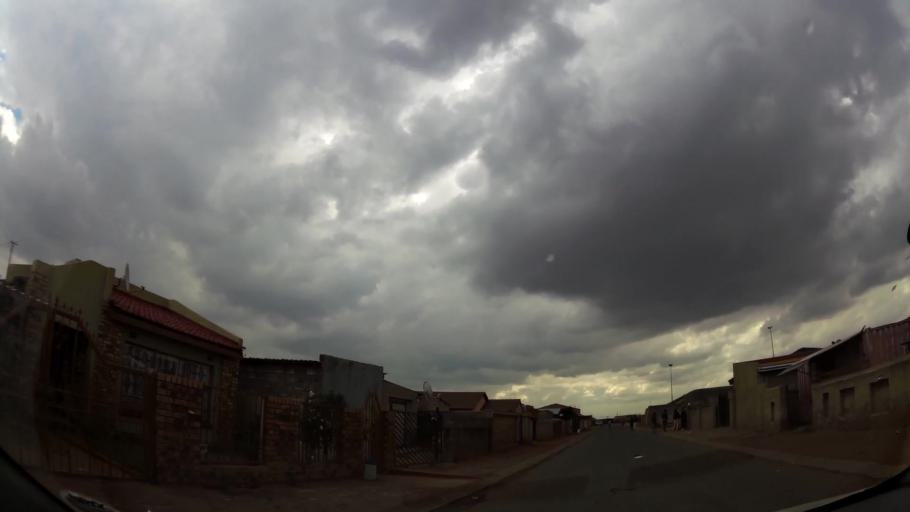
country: ZA
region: Gauteng
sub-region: Ekurhuleni Metropolitan Municipality
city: Germiston
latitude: -26.3682
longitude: 28.1599
